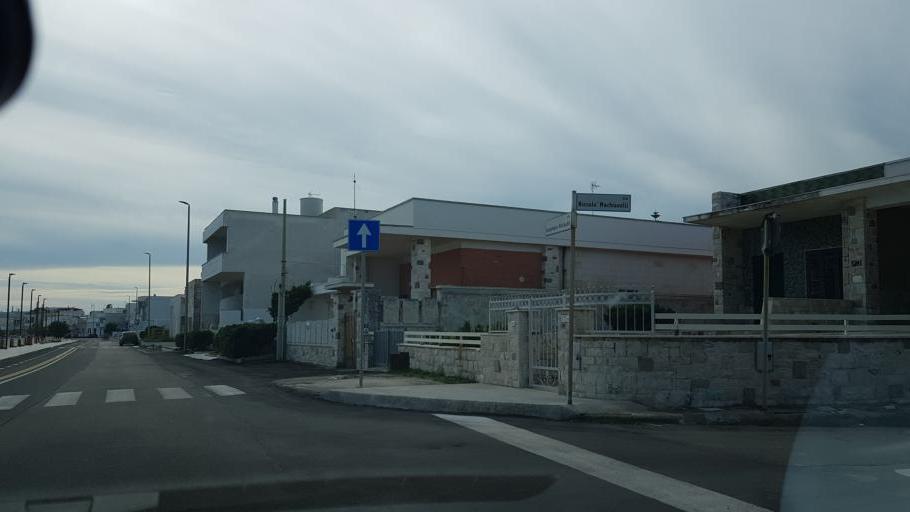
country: IT
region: Apulia
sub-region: Provincia di Lecce
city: Borgagne
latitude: 40.3050
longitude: 18.3990
